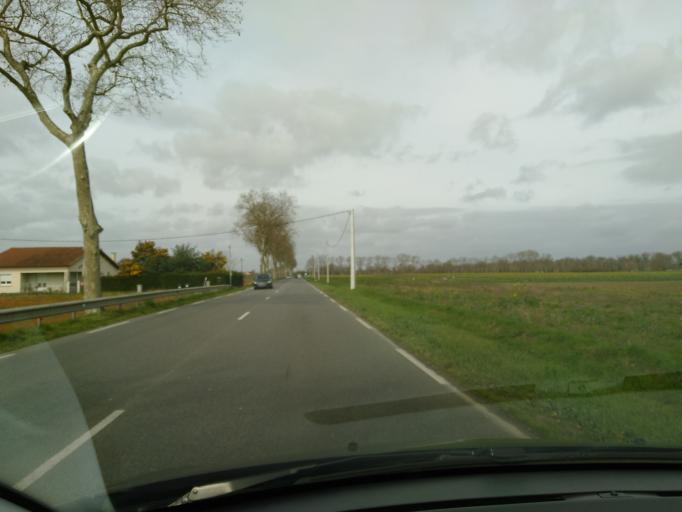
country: FR
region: Midi-Pyrenees
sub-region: Departement de la Haute-Garonne
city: Seilh
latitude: 43.7008
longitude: 1.3470
